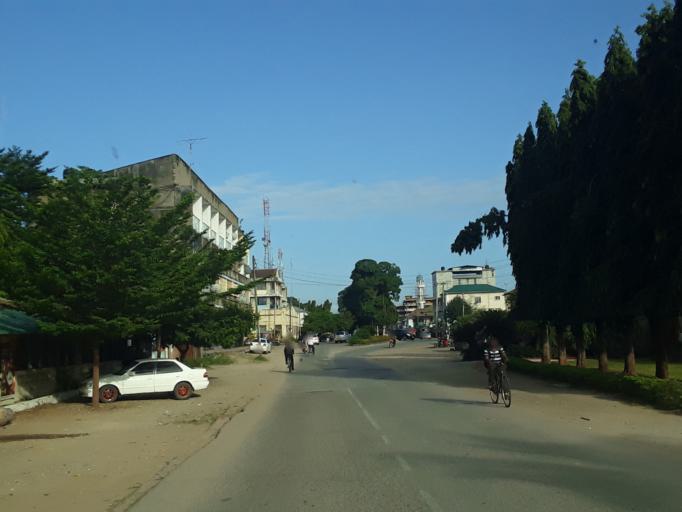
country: TZ
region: Tanga
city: Tanga
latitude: -5.0728
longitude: 39.1074
